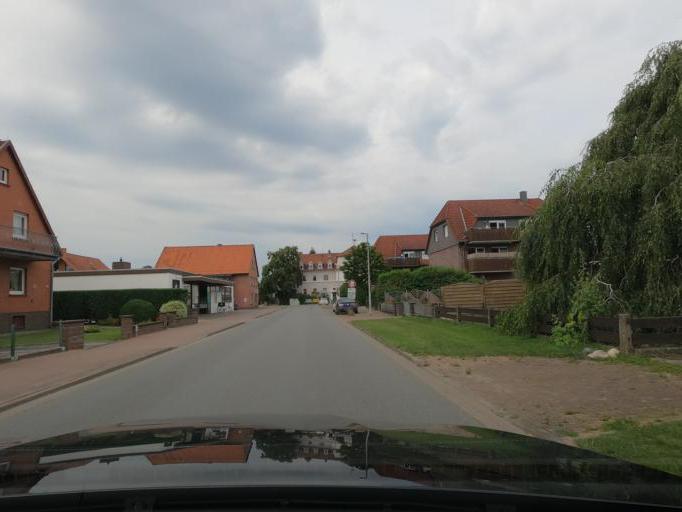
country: DE
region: Lower Saxony
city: Garbsen-Mitte
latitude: 52.4619
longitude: 9.6033
